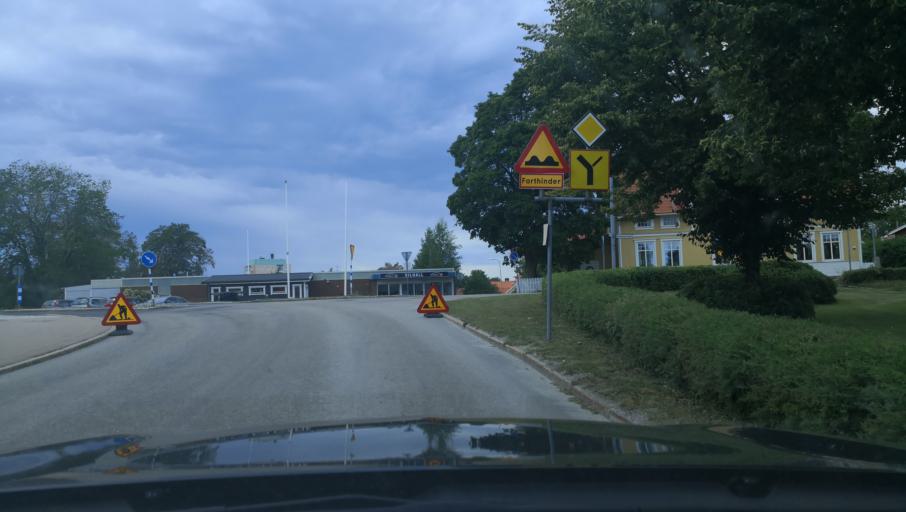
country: SE
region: Vaestmanland
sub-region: Fagersta Kommun
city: Fagersta
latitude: 59.9883
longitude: 15.8211
